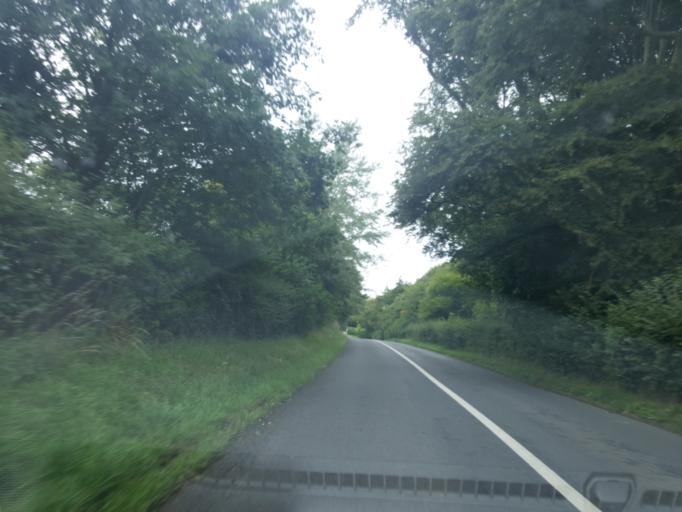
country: IE
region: Leinster
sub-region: Kildare
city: Kilcullen
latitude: 53.1203
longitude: -6.7186
